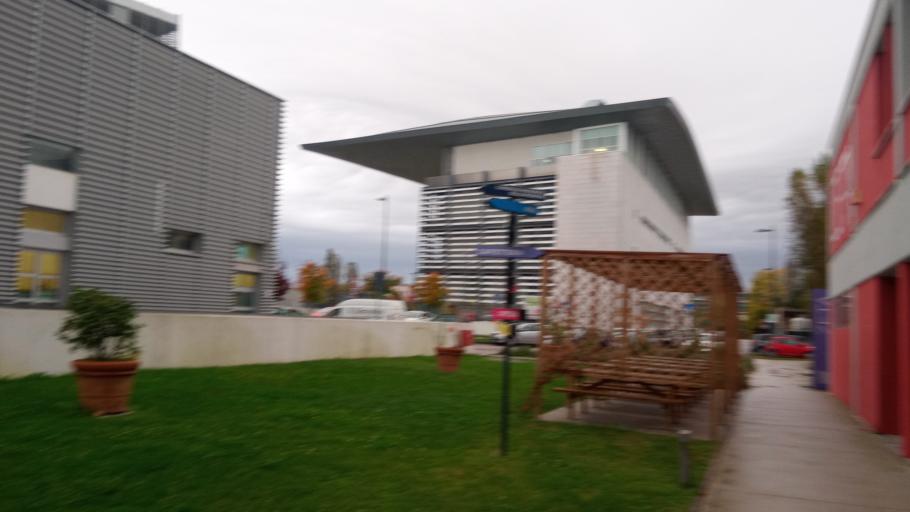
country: IT
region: Veneto
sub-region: Provincia di Venezia
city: Mestre
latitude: 45.4786
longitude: 12.2555
